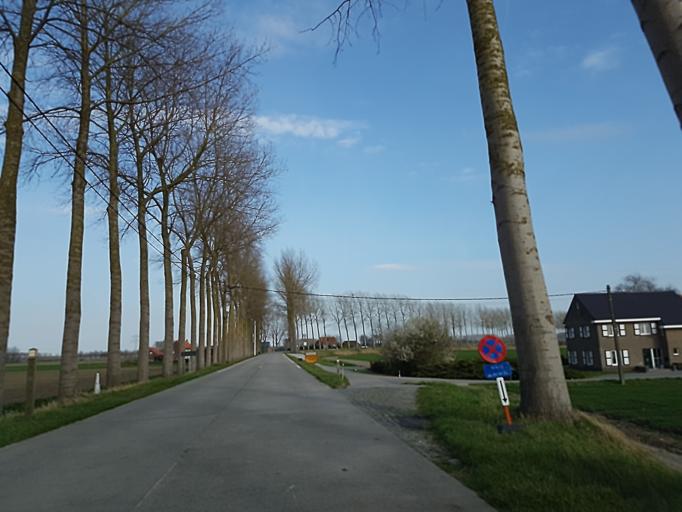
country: BE
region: Flanders
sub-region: Provincie Oost-Vlaanderen
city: Assenede
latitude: 51.2807
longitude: 3.6863
